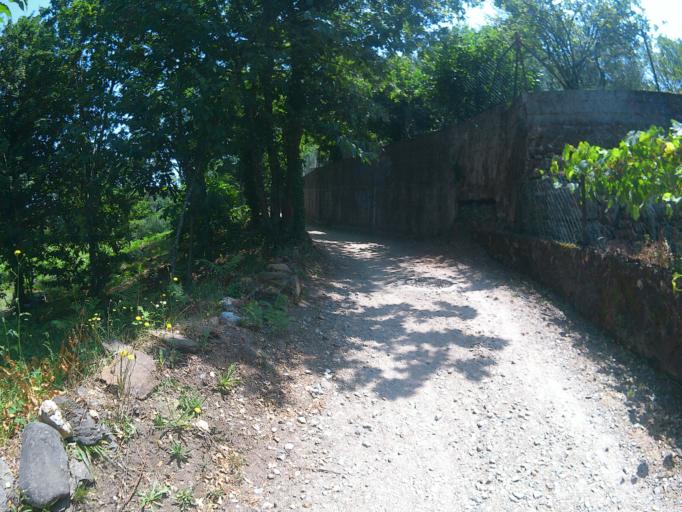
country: PT
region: Viana do Castelo
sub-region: Ponte de Lima
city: Ponte de Lima
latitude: 41.7743
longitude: -8.5653
